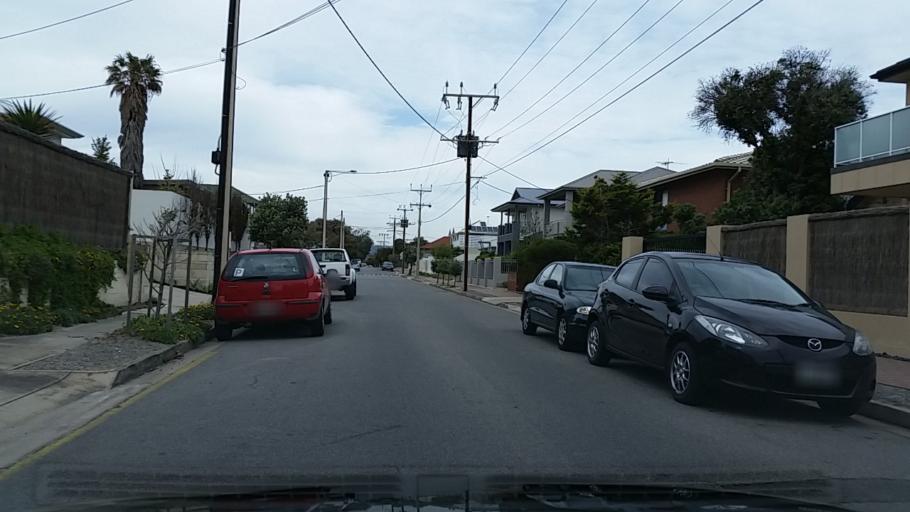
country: AU
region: South Australia
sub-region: Holdfast Bay
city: North Brighton
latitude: -35.0092
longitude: 138.5130
